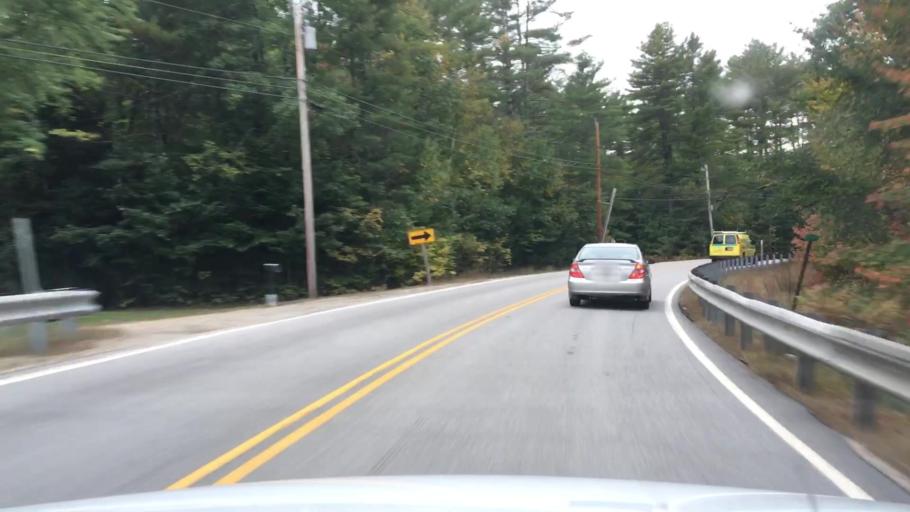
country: US
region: Maine
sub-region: Cumberland County
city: Harrison
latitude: 44.2116
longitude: -70.6644
